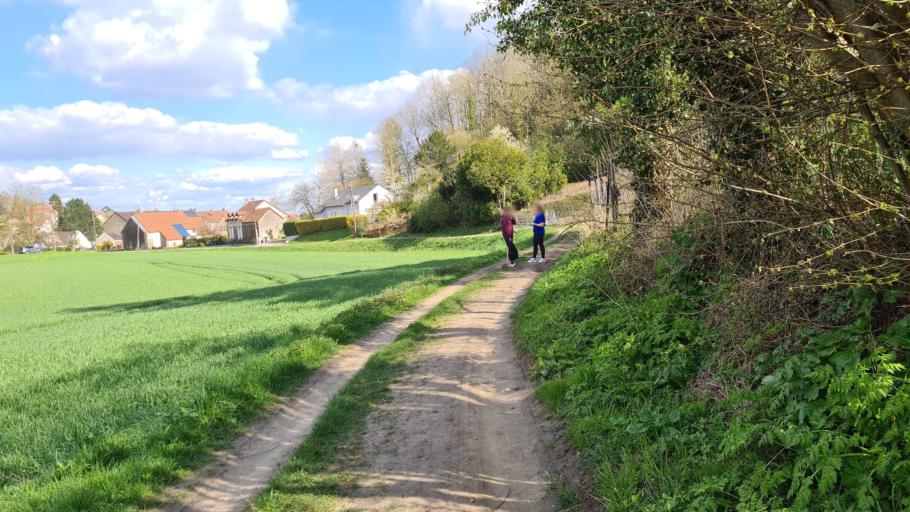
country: FR
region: Picardie
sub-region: Departement de l'Aisne
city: Laon
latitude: 49.5593
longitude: 3.6192
